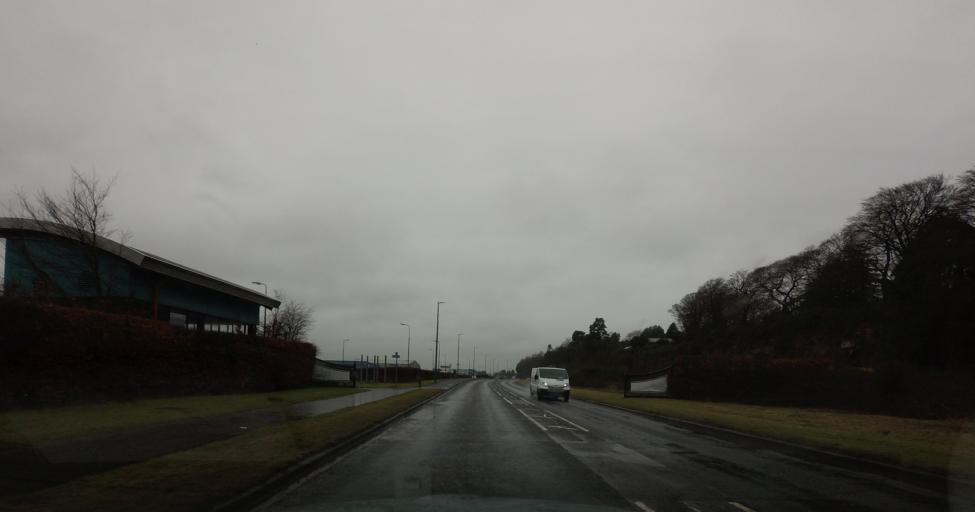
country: GB
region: Scotland
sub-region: Dundee City
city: Dundee
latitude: 56.4543
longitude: -3.0114
